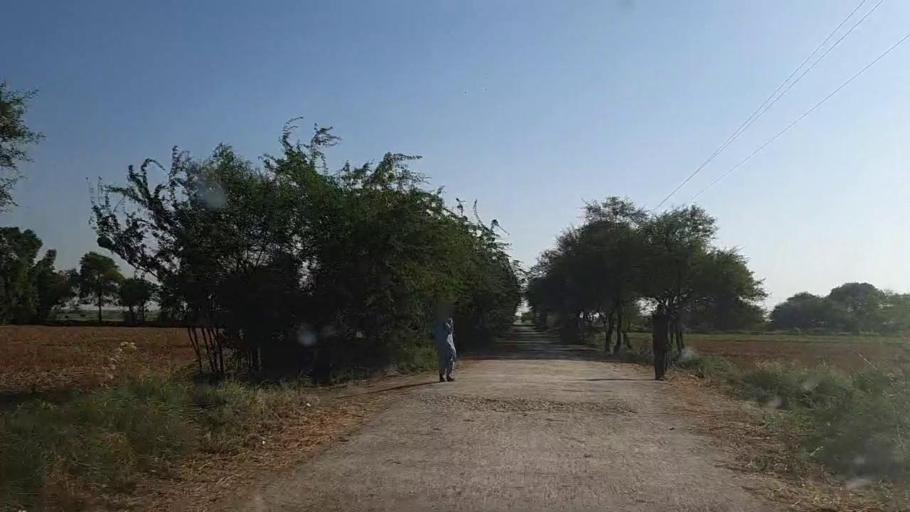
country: PK
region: Sindh
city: Daro Mehar
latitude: 24.6459
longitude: 68.0751
